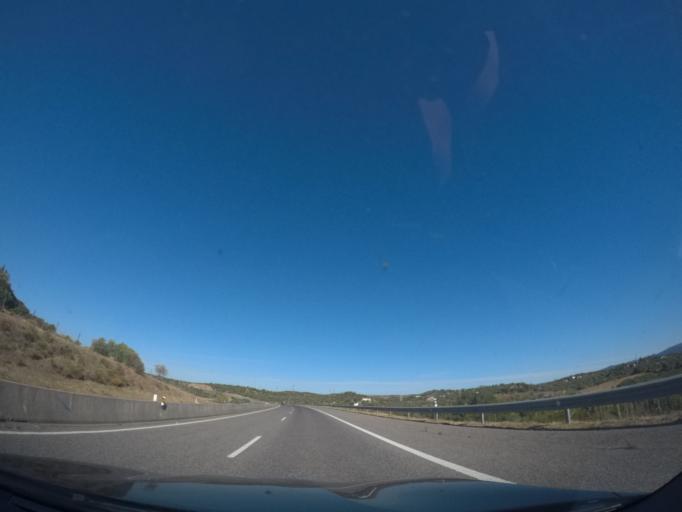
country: PT
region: Faro
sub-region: Portimao
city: Alvor
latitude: 37.1832
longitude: -8.5897
